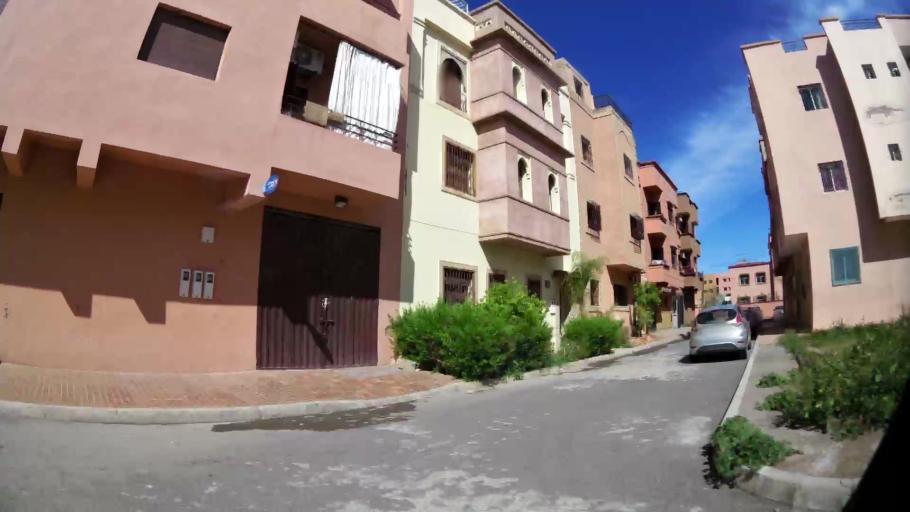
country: MA
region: Marrakech-Tensift-Al Haouz
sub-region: Marrakech
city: Marrakesh
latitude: 31.6707
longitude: -8.0248
